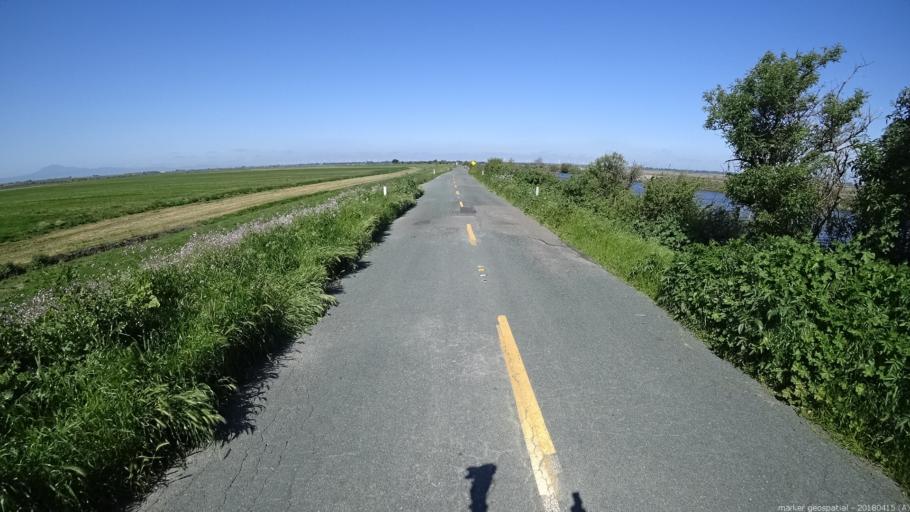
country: US
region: California
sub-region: Solano County
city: Rio Vista
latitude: 38.1177
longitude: -121.6395
